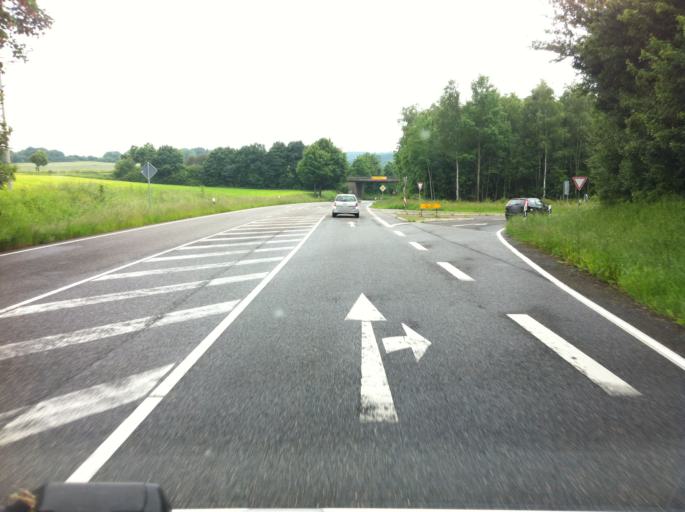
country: DE
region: North Rhine-Westphalia
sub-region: Regierungsbezirk Koln
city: Nettersheim
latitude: 50.4936
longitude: 6.6194
